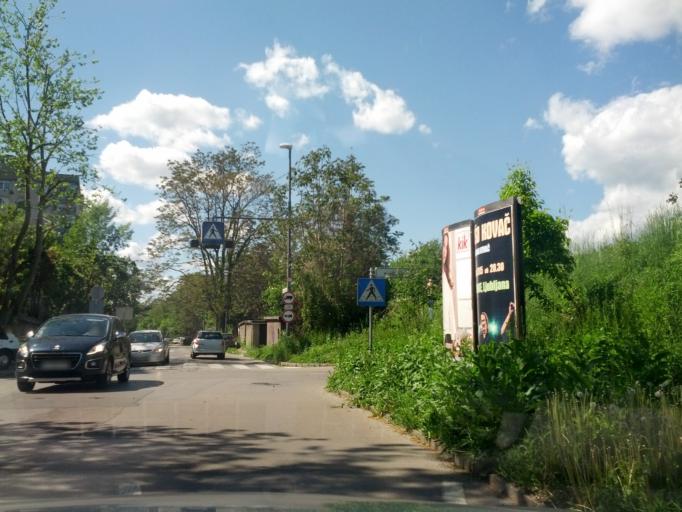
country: SI
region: Ljubljana
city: Ljubljana
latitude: 46.0573
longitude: 14.5272
